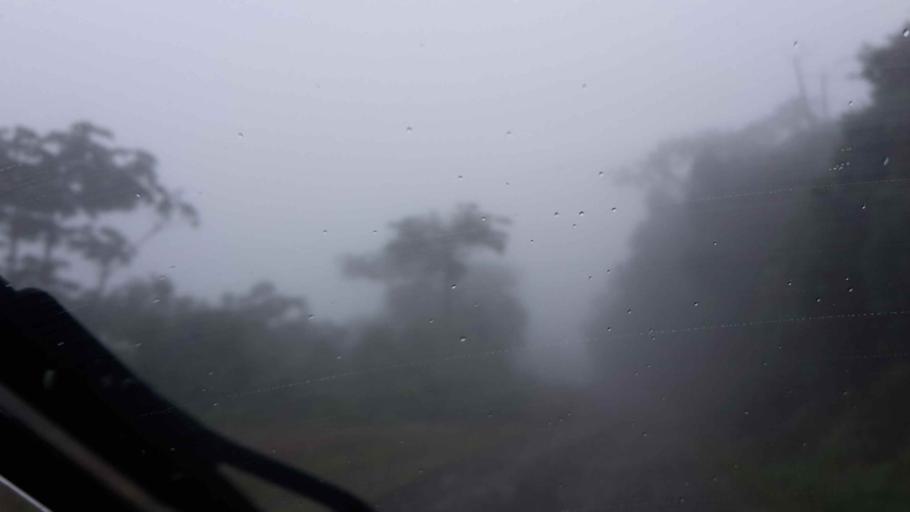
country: BO
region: Cochabamba
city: Colomi
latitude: -17.0914
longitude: -65.9867
